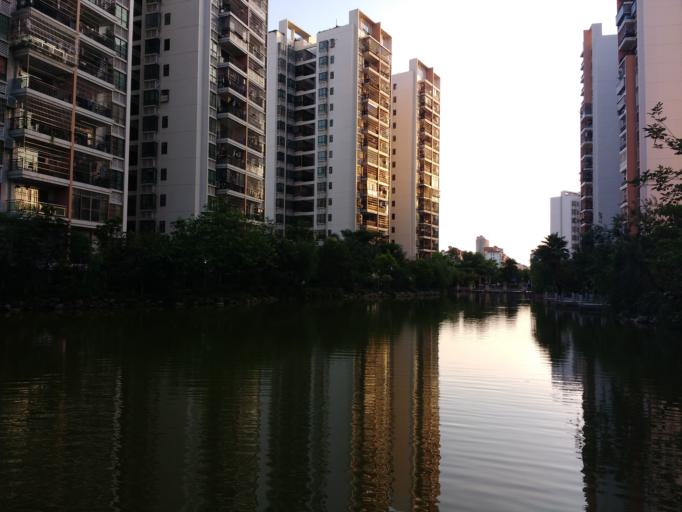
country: CN
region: Guangdong
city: Jianghai
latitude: 22.5710
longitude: 113.1113
